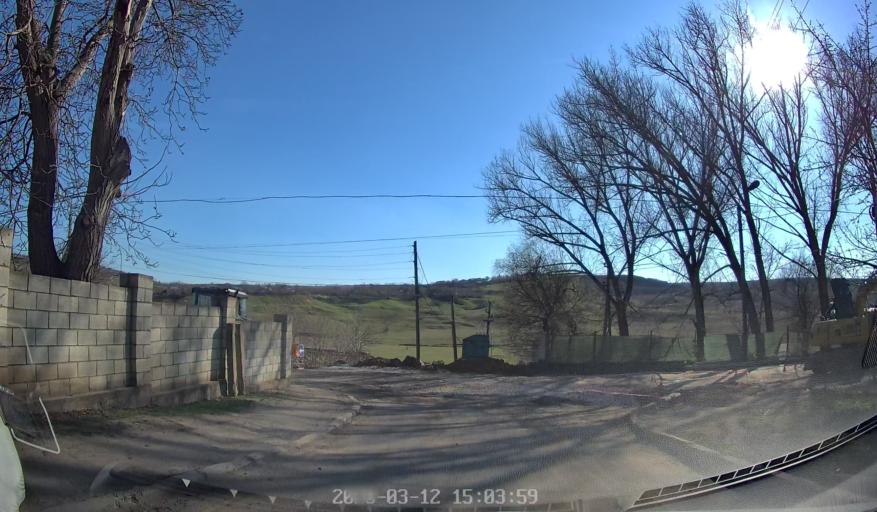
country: MD
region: Telenesti
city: Cocieri
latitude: 47.2212
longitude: 29.0191
